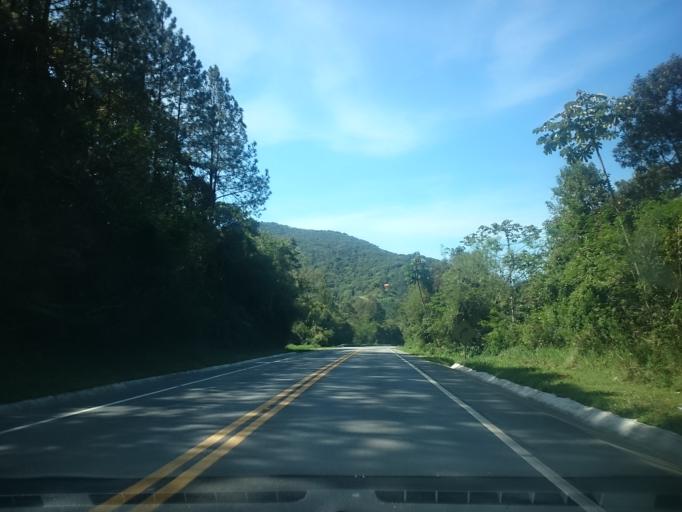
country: BR
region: Santa Catarina
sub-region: Santo Amaro Da Imperatriz
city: Santo Amaro da Imperatriz
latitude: -27.7149
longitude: -48.8679
